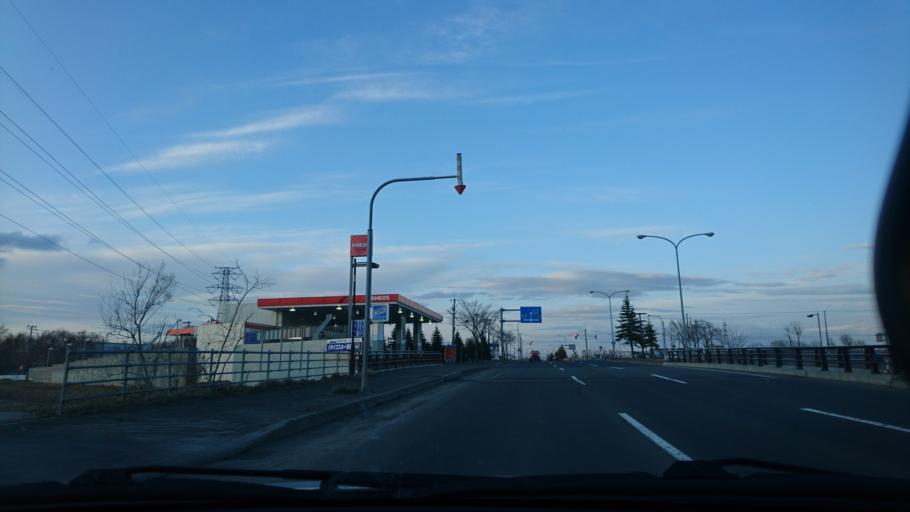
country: JP
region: Hokkaido
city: Sapporo
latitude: 43.1219
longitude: 141.4128
